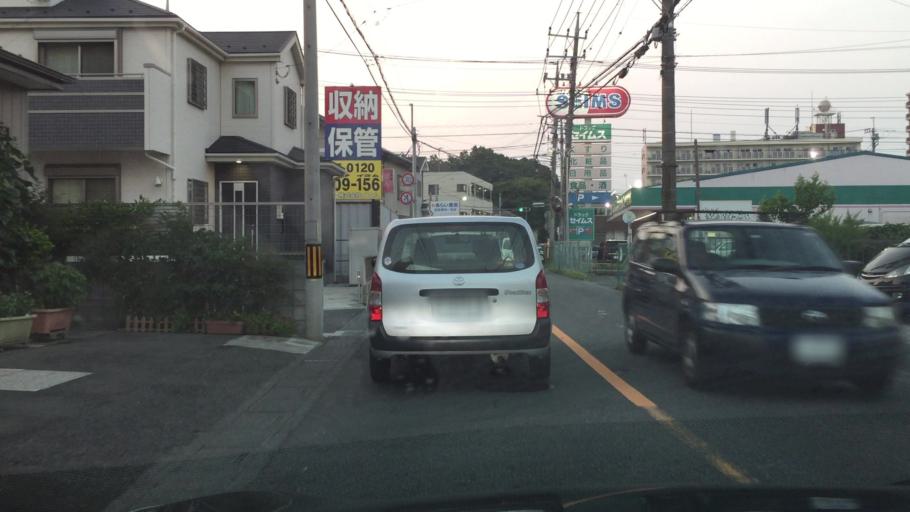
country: JP
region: Saitama
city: Yono
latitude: 35.9137
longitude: 139.6053
